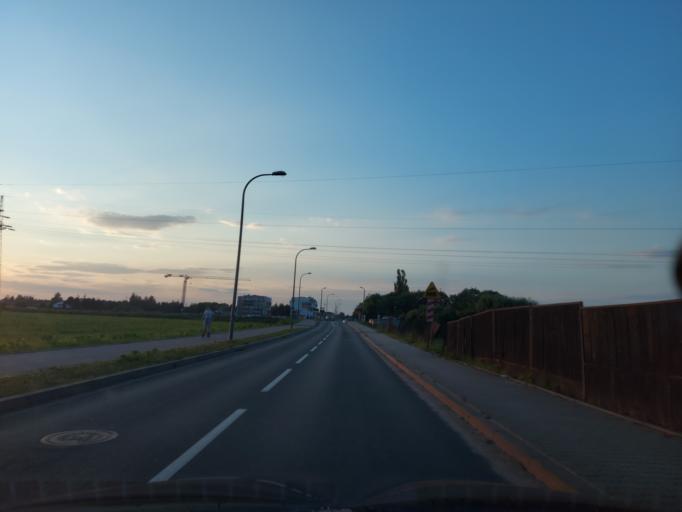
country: PL
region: Masovian Voivodeship
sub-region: Powiat piaseczynski
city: Piaseczno
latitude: 52.0841
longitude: 21.0143
